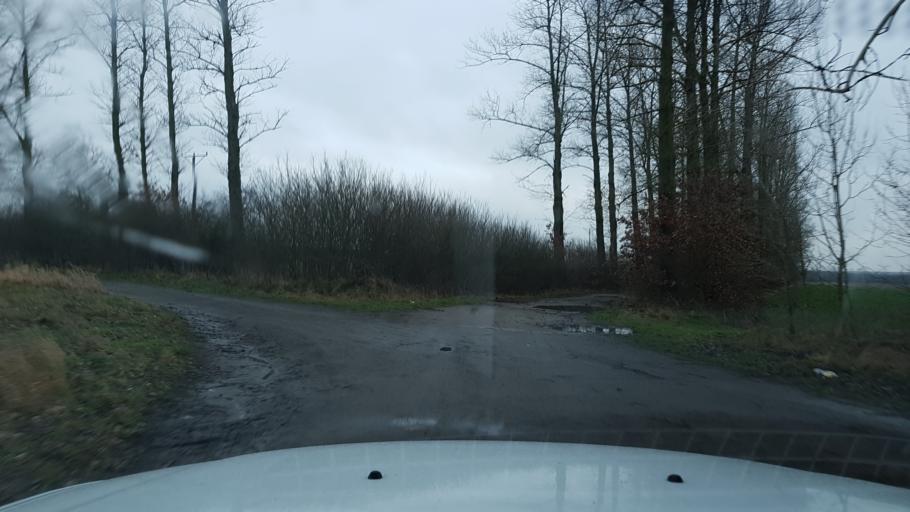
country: PL
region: West Pomeranian Voivodeship
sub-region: Powiat gryficki
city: Brojce
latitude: 53.9852
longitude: 15.3116
